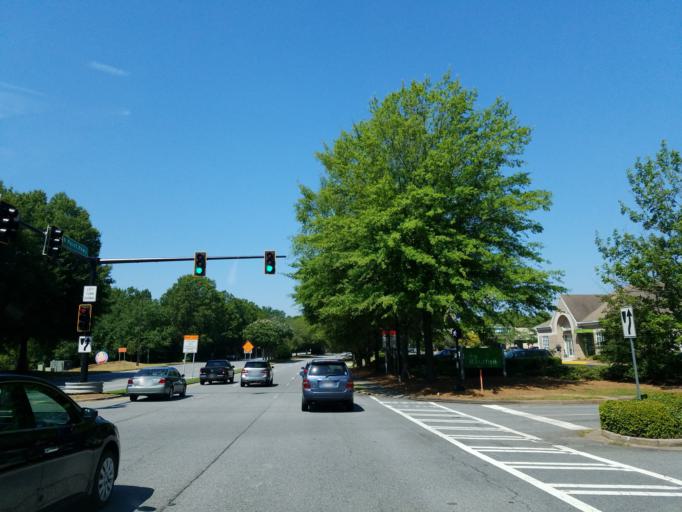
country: US
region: Georgia
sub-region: Fulton County
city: Alpharetta
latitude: 34.0454
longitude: -84.2941
